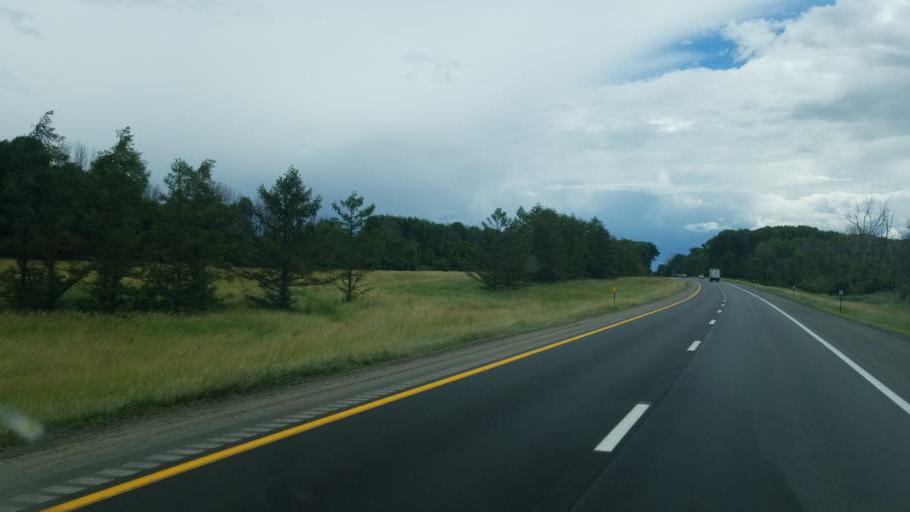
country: US
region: New York
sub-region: Livingston County
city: Caledonia
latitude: 43.0301
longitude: -77.8319
